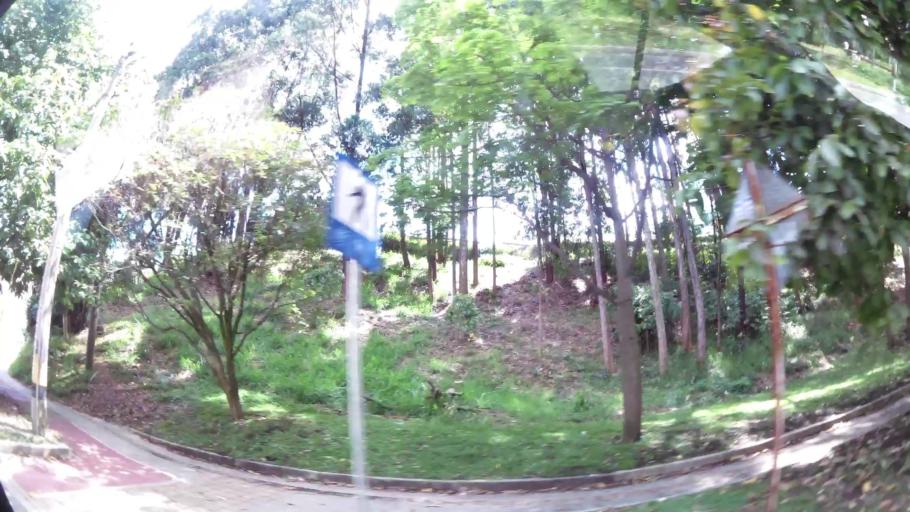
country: CO
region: Antioquia
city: Sabaneta
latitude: 6.1565
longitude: -75.6260
